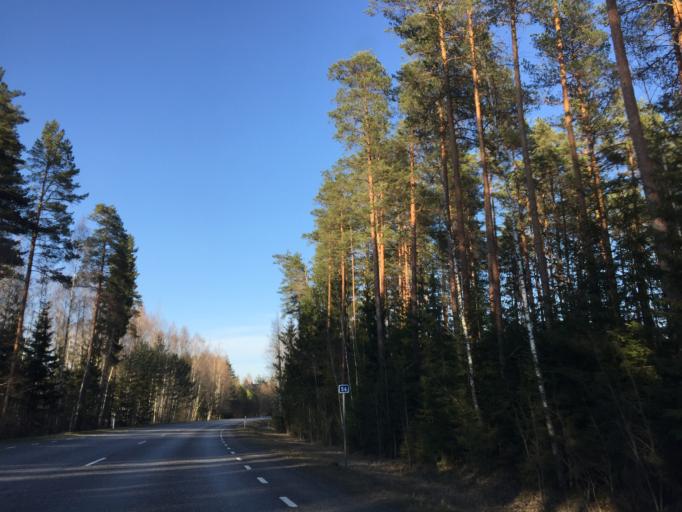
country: EE
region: Valgamaa
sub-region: Torva linn
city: Torva
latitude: 58.1250
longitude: 26.1386
